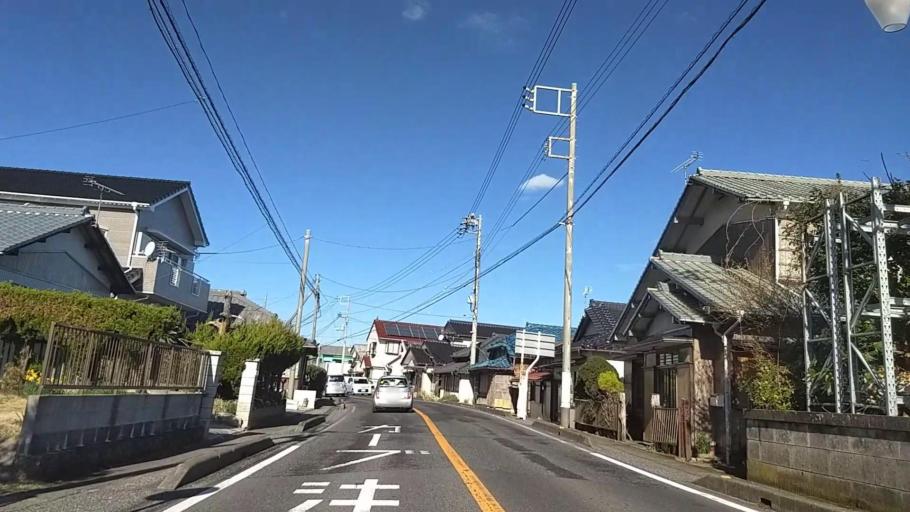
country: JP
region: Chiba
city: Katsuura
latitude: 35.1792
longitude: 140.3478
